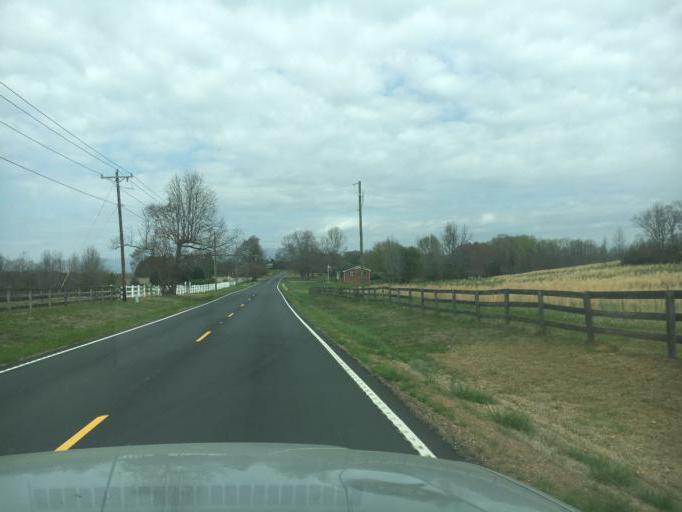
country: US
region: South Carolina
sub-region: Spartanburg County
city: Inman Mills
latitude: 35.0704
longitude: -82.1764
